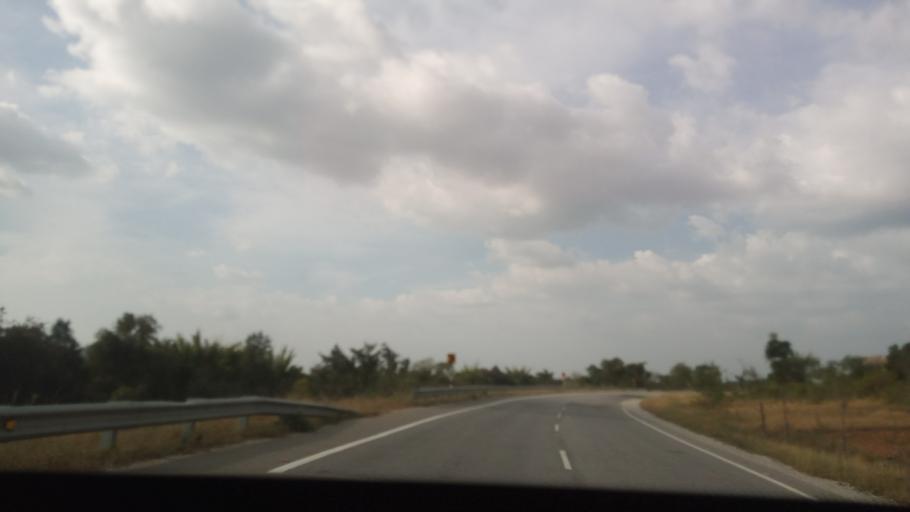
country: IN
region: Karnataka
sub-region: Tumkur
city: Kunigal
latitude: 12.8208
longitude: 77.0276
